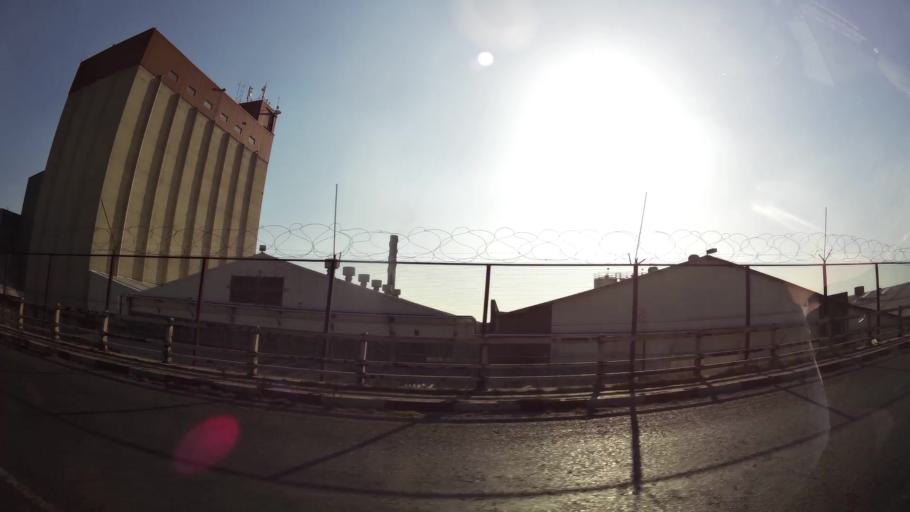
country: ZA
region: Gauteng
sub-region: West Rand District Municipality
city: Randfontein
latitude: -26.1631
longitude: 27.7130
